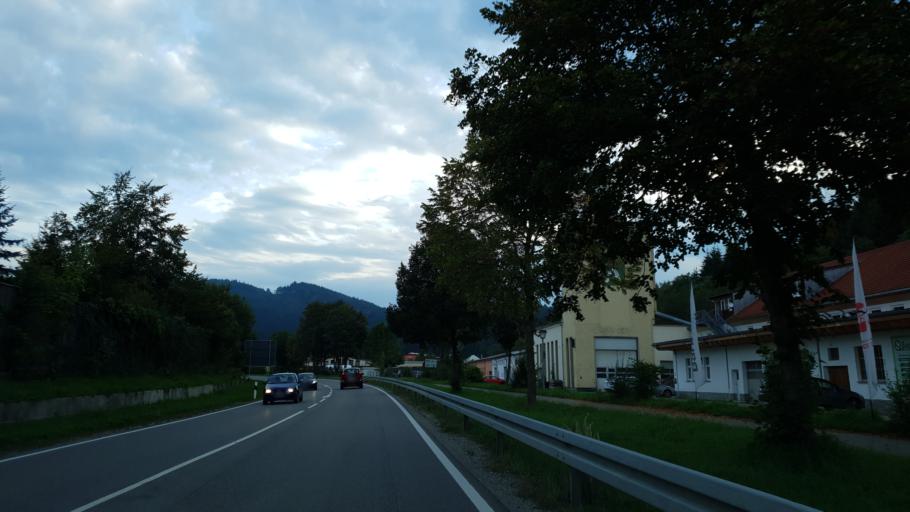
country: DE
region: Bavaria
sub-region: Swabia
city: Weitnau
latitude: 47.6600
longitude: 10.0914
